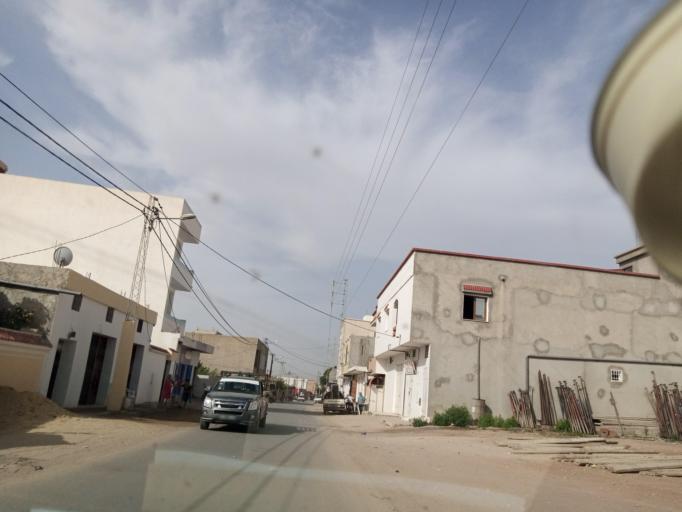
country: TN
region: Al Qasrayn
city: Kasserine
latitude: 35.2144
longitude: 8.8976
